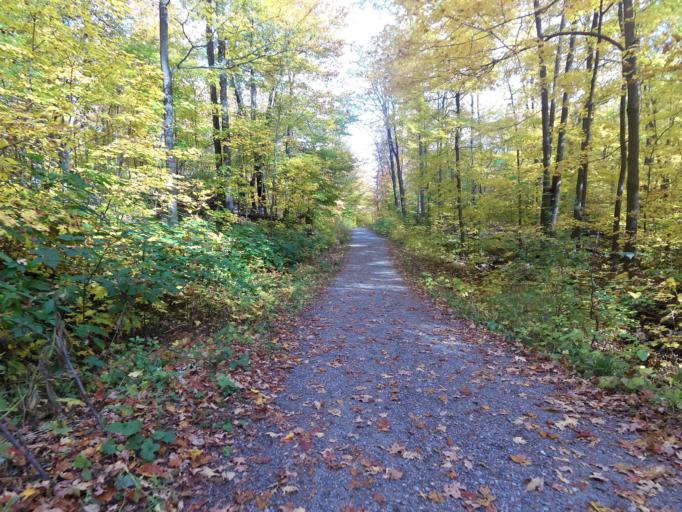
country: CA
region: Quebec
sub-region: Outaouais
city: Gatineau
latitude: 45.4978
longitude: -75.8411
